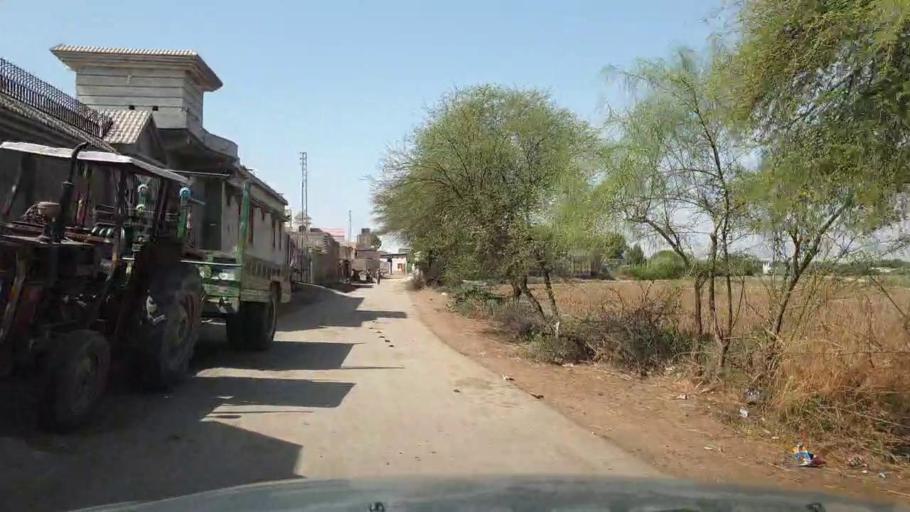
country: PK
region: Sindh
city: Tando Muhammad Khan
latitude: 25.1493
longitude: 68.4373
